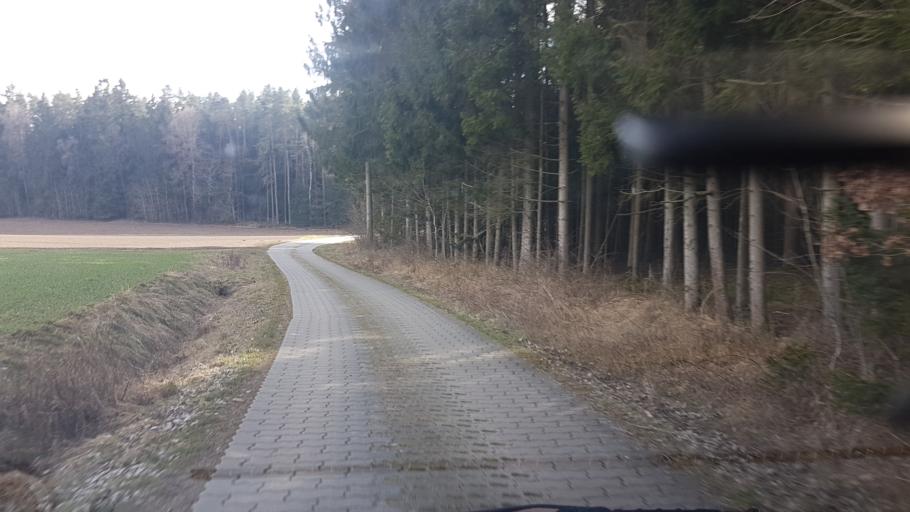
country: DE
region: Bavaria
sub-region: Upper Franconia
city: Stadelhofen
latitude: 49.9968
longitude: 11.2318
